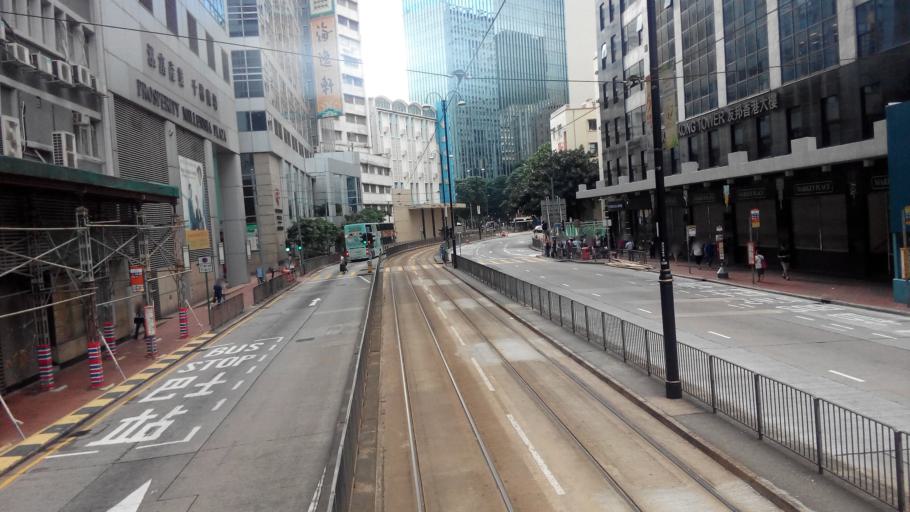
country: HK
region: Kowloon City
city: Kowloon
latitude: 22.2916
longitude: 114.2078
